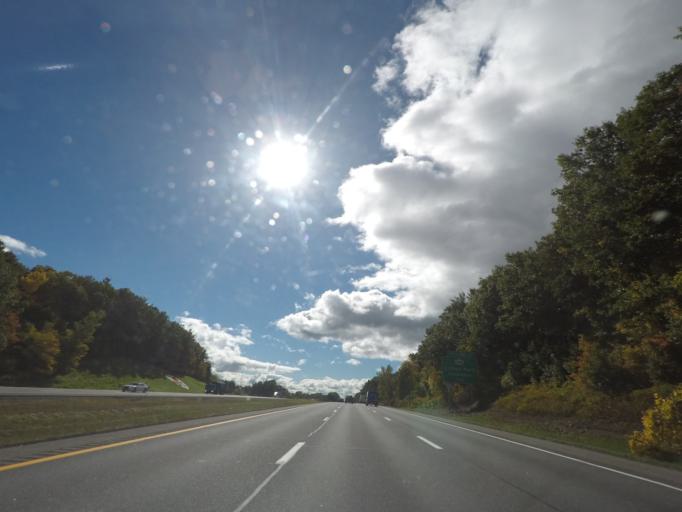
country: US
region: New York
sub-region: Saratoga County
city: Country Knolls
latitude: 42.8807
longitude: -73.7784
